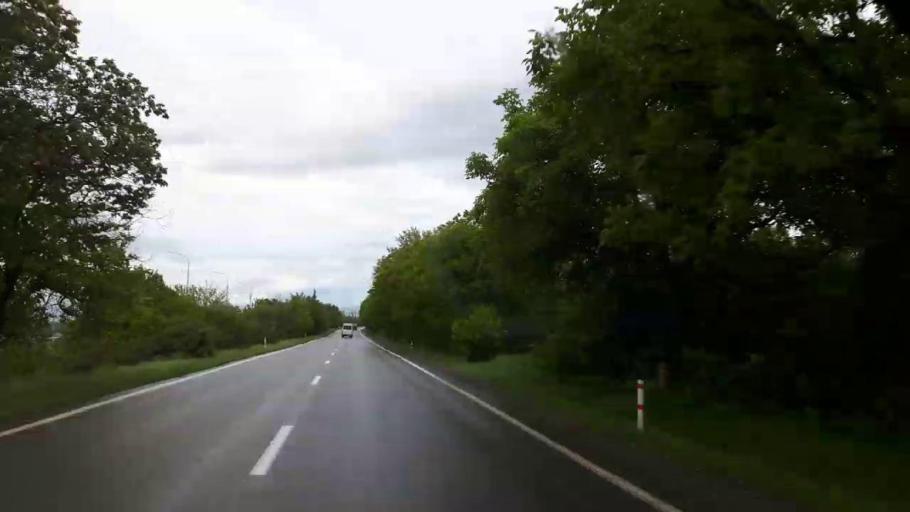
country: GE
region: Shida Kartli
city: Kaspi
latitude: 41.9532
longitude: 44.4941
